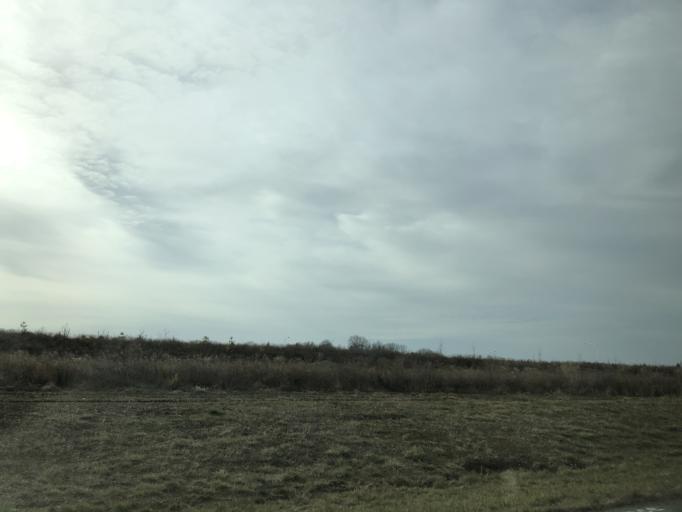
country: US
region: Delaware
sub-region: New Castle County
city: Middletown
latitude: 39.5261
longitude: -75.6700
